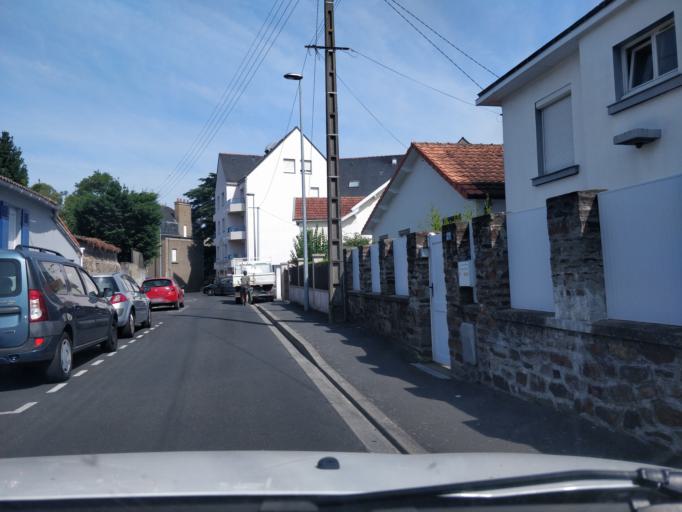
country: FR
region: Pays de la Loire
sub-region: Departement de la Loire-Atlantique
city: Saint-Sebastien-sur-Loire
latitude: 47.2085
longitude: -1.5010
